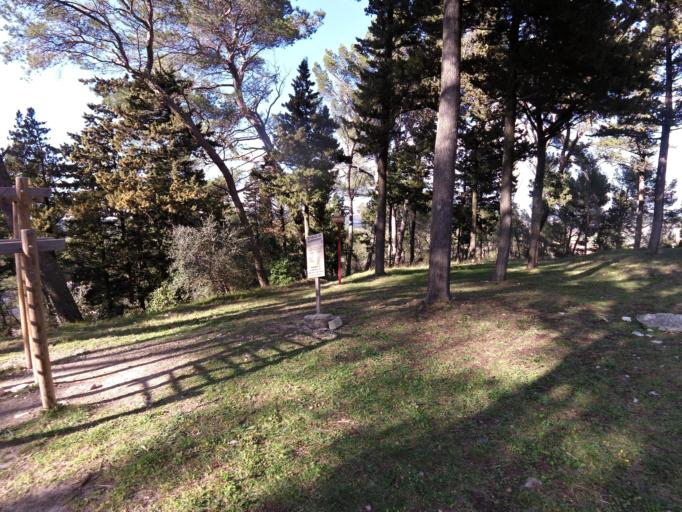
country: FR
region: Languedoc-Roussillon
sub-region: Departement du Gard
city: Calvisson
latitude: 43.7824
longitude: 4.1883
